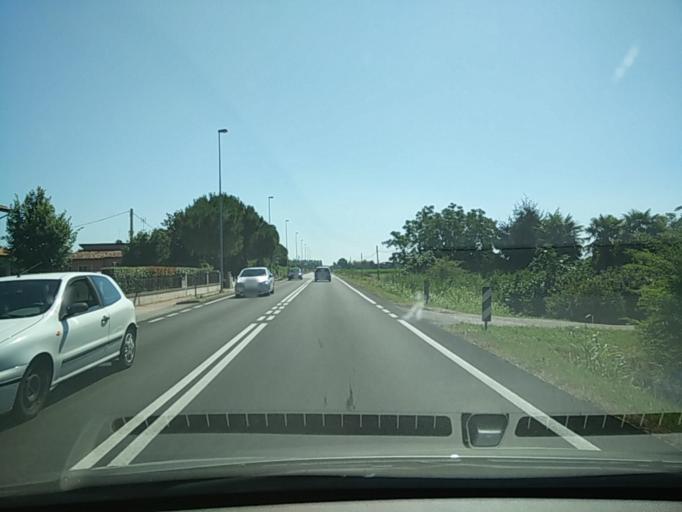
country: IT
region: Veneto
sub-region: Provincia di Venezia
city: Crepaldo
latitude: 45.6365
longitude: 12.6949
